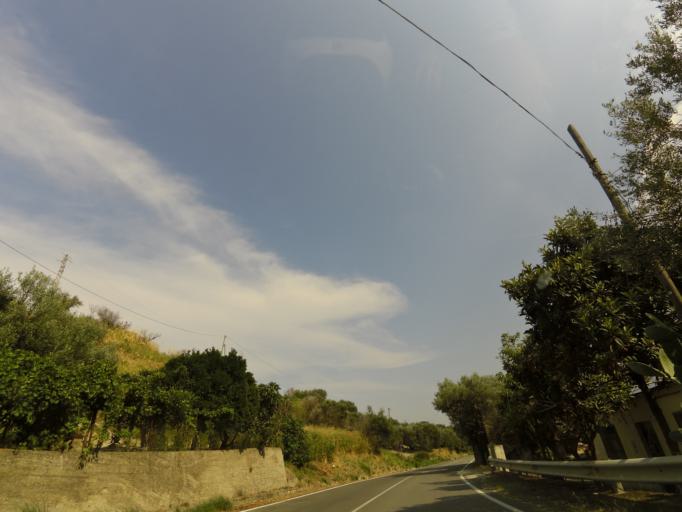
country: IT
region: Calabria
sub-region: Provincia di Reggio Calabria
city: Monasterace
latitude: 38.4533
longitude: 16.5284
